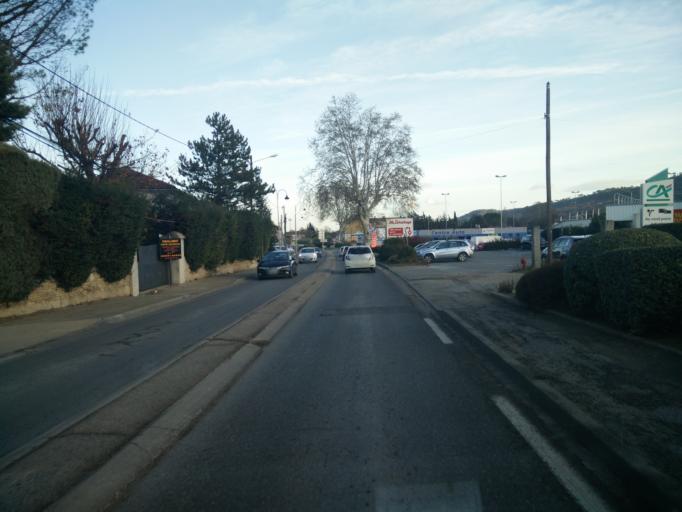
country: FR
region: Provence-Alpes-Cote d'Azur
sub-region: Departement du Var
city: La Celle
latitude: 43.4082
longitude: 6.0474
